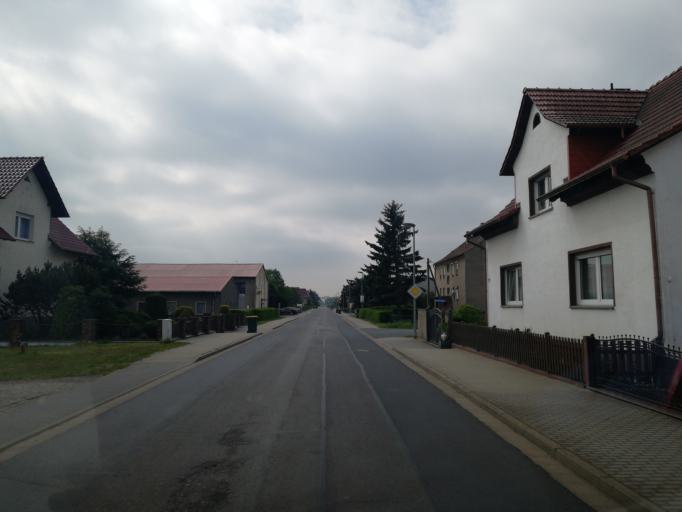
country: DE
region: Saxony
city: Beilrode
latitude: 51.6383
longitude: 13.1200
